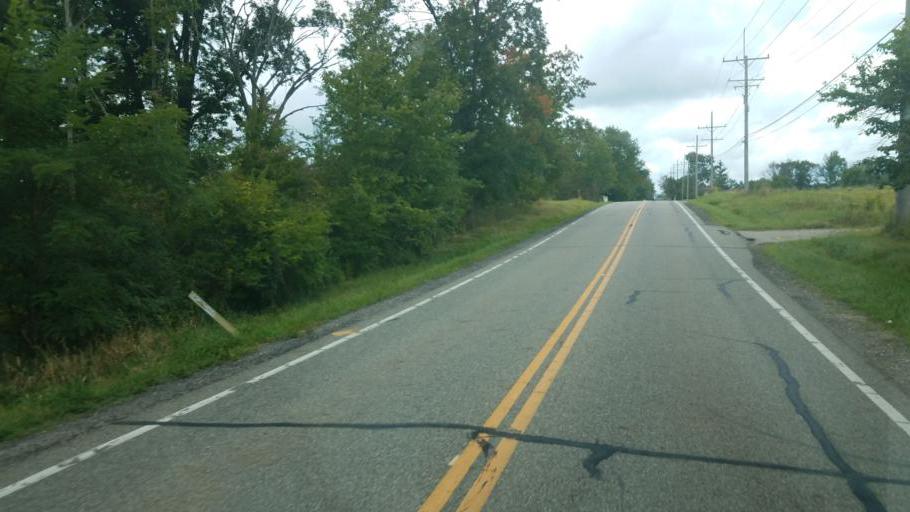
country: US
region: Ohio
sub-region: Geauga County
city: Burton
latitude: 41.5246
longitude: -81.1441
